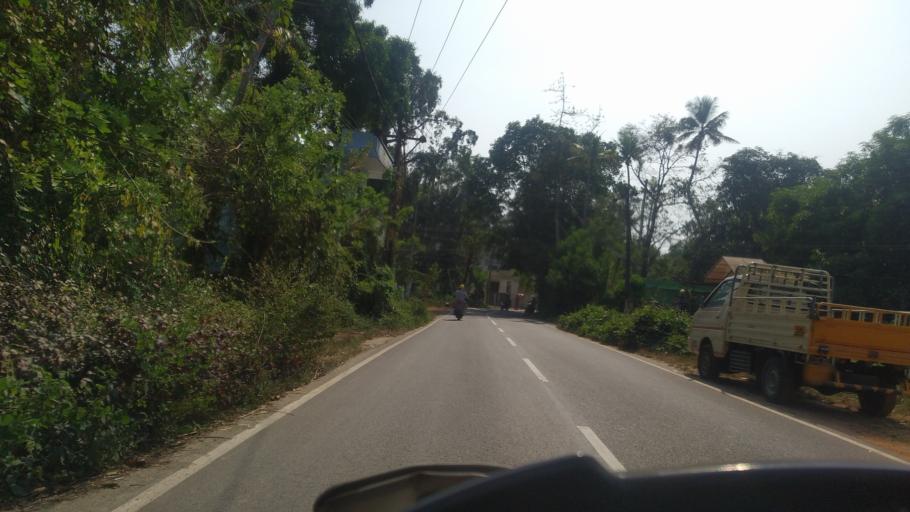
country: IN
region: Kerala
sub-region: Thrissur District
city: Kodungallur
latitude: 10.2110
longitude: 76.1879
